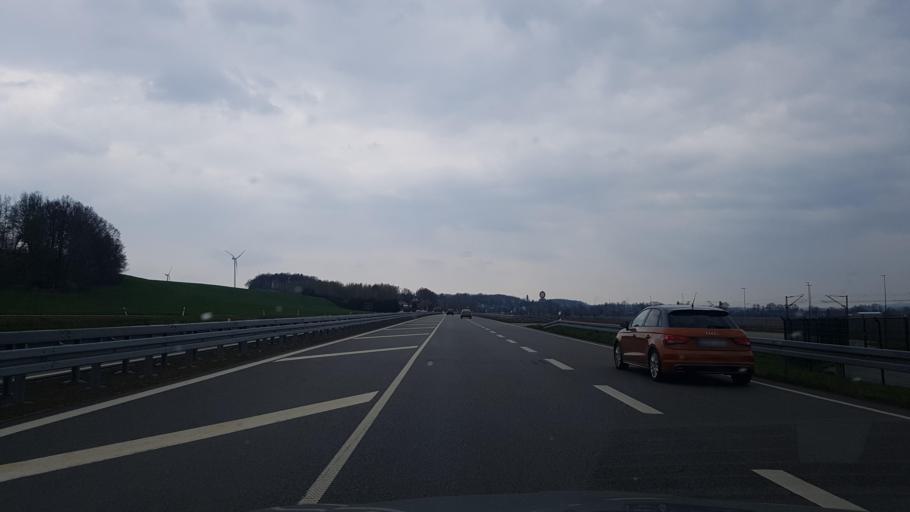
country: DE
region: Saxony
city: Dennheritz
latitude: 50.8044
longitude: 12.4839
